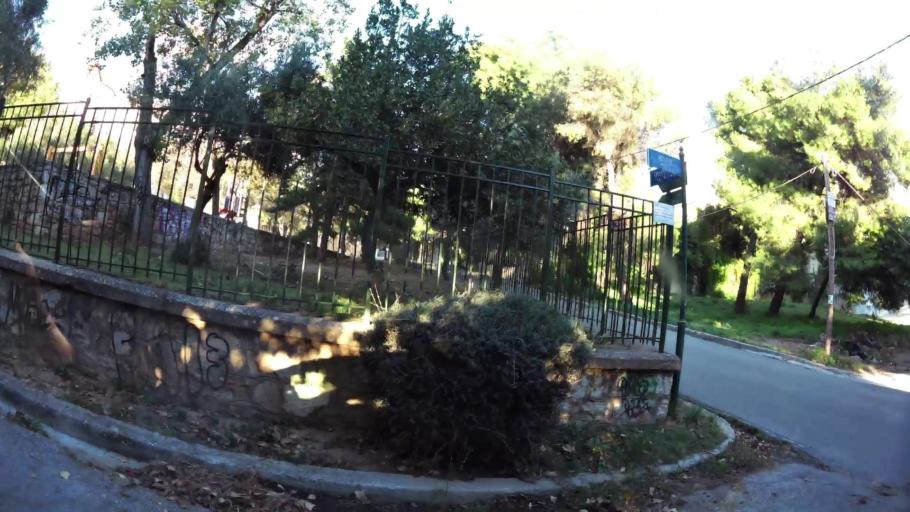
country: GR
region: Attica
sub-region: Nomarchia Athinas
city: Nea Erythraia
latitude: 38.0859
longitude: 23.8314
